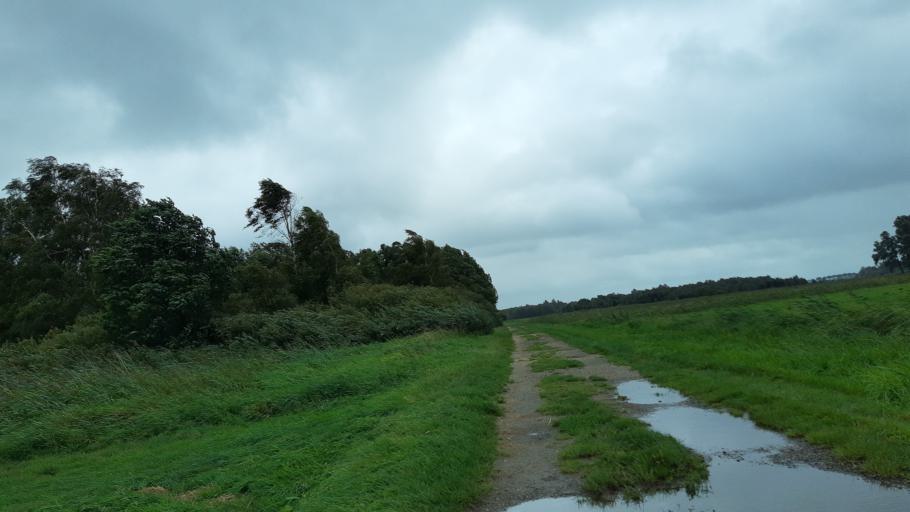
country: NL
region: Overijssel
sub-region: Gemeente Steenwijkerland
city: Blokzijl
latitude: 52.7590
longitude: 5.9746
